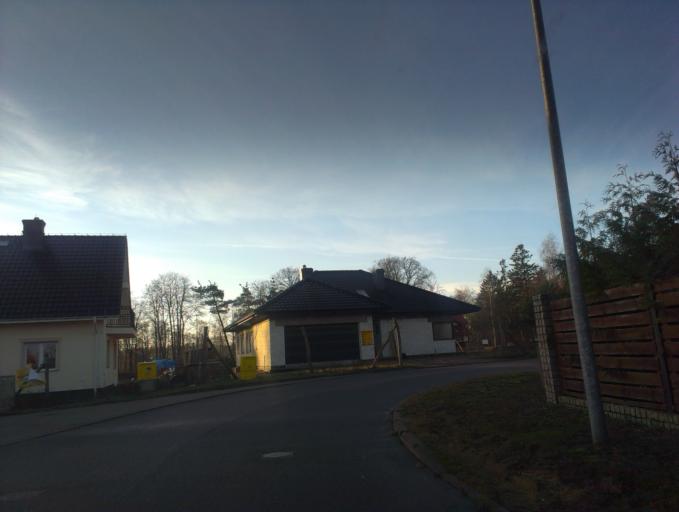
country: PL
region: West Pomeranian Voivodeship
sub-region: Powiat szczecinecki
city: Szczecinek
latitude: 53.7175
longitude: 16.6579
